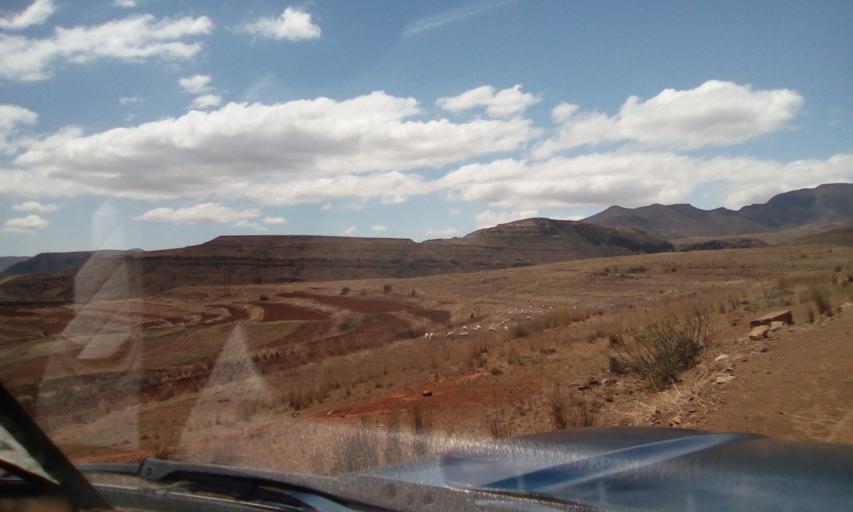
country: LS
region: Qacha's Nek
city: Qacha's Nek
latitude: -30.0642
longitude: 28.6256
